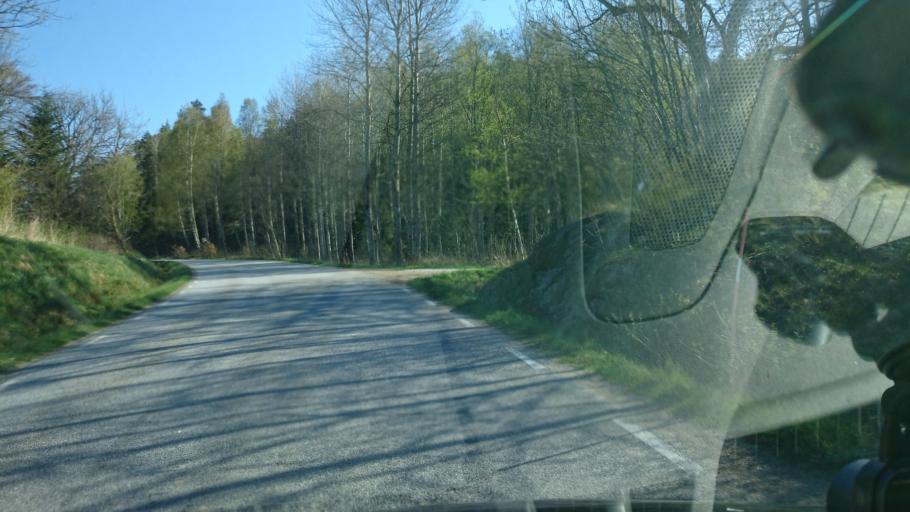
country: SE
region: Vaestra Goetaland
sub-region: Munkedals Kommun
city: Munkedal
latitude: 58.4161
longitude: 11.6846
